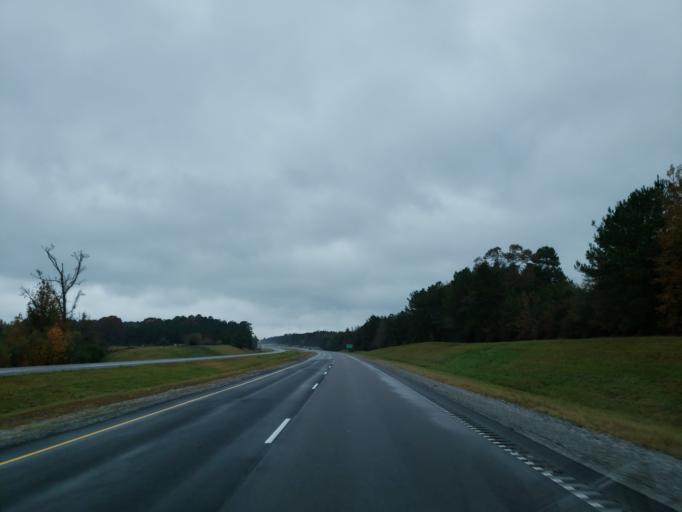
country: US
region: Mississippi
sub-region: Clarke County
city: Quitman
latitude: 32.0454
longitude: -88.6769
